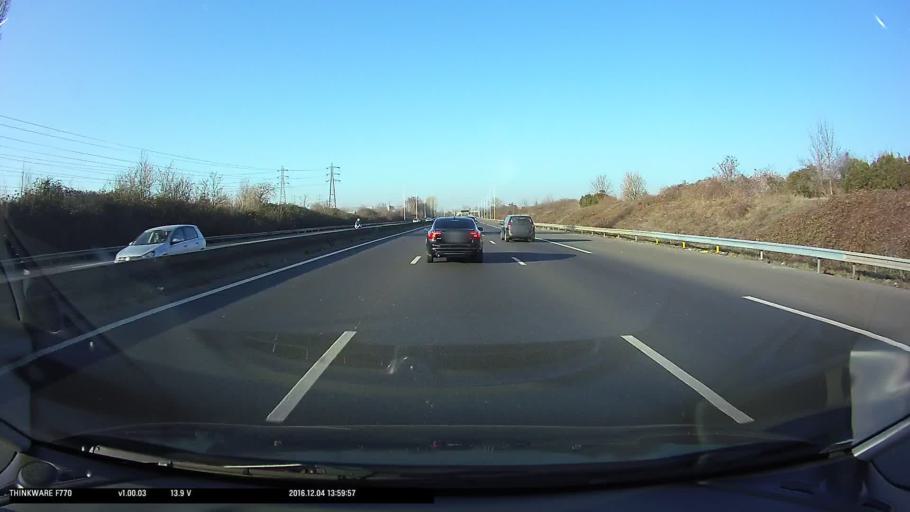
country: FR
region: Ile-de-France
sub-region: Departement du Val-d'Oise
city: Pierrelaye
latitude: 49.0239
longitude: 2.1335
